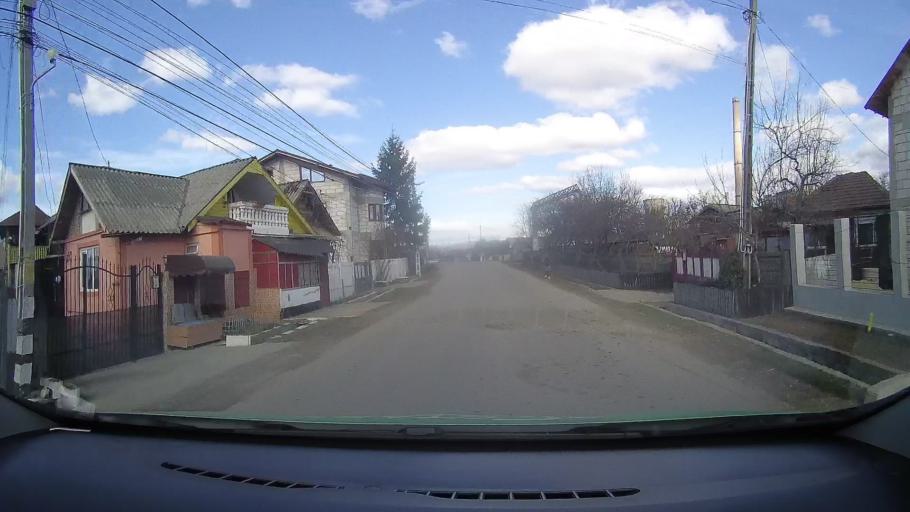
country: RO
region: Dambovita
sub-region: Comuna Doicesti
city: Doicesti
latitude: 44.9955
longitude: 25.3926
